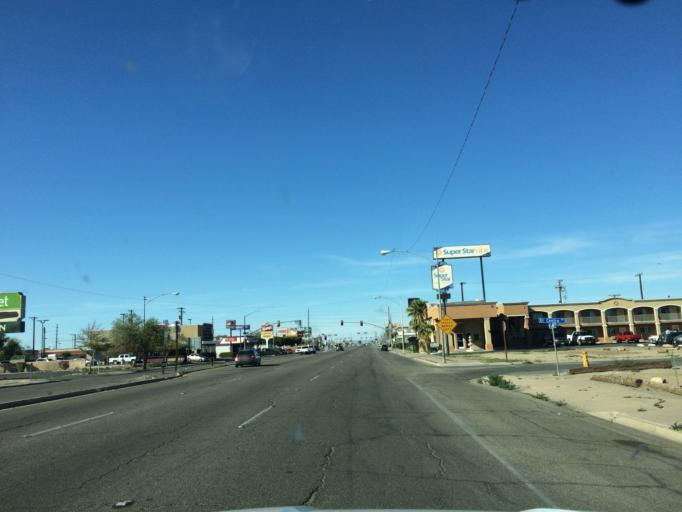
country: US
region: California
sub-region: Imperial County
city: El Centro
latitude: 32.7971
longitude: -115.5698
